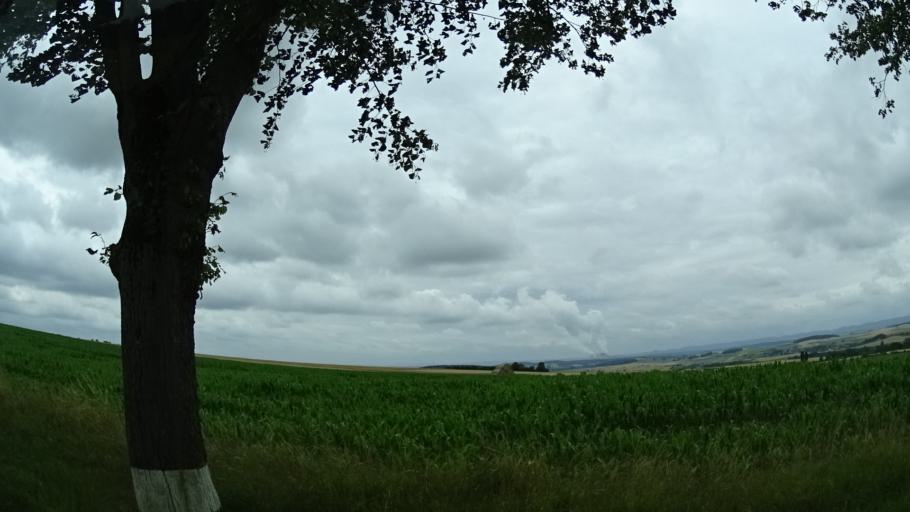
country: LU
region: Grevenmacher
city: Schengen
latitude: 49.4793
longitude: 6.3331
